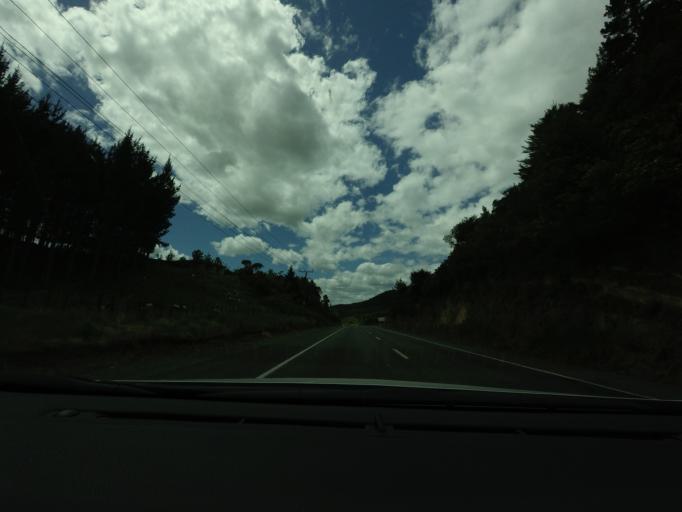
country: NZ
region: Bay of Plenty
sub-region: Rotorua District
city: Rotorua
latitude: -38.3250
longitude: 176.3702
